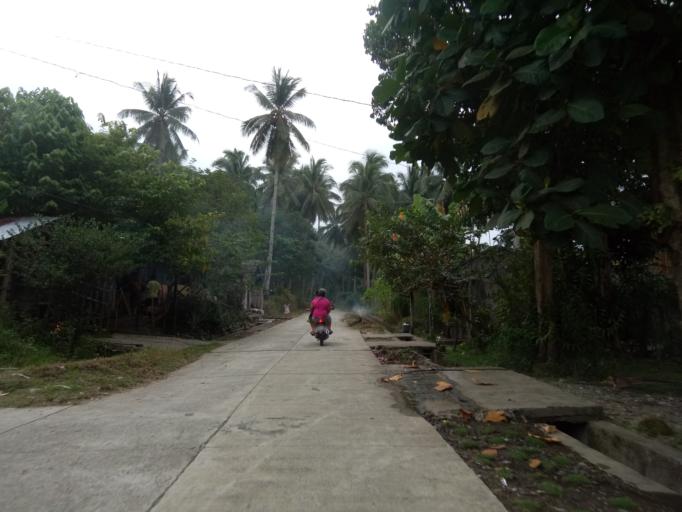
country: PH
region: Caraga
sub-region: Province of Surigao del Norte
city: Tubod
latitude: 9.5665
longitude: 125.5674
